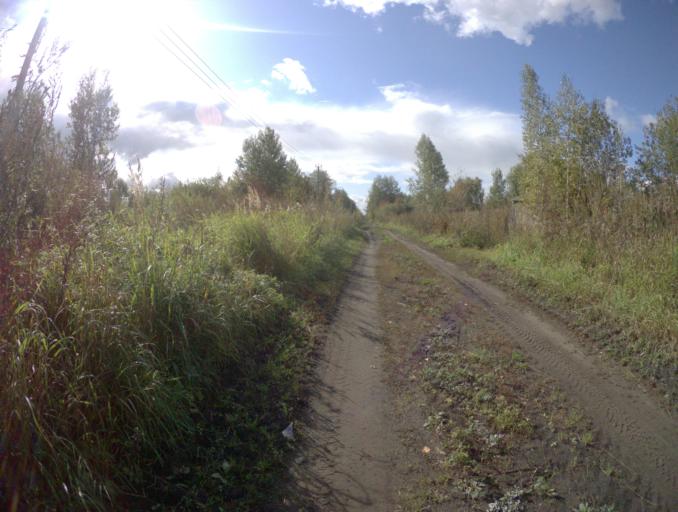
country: RU
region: Moskovskaya
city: Kerva
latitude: 55.7058
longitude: 39.5945
